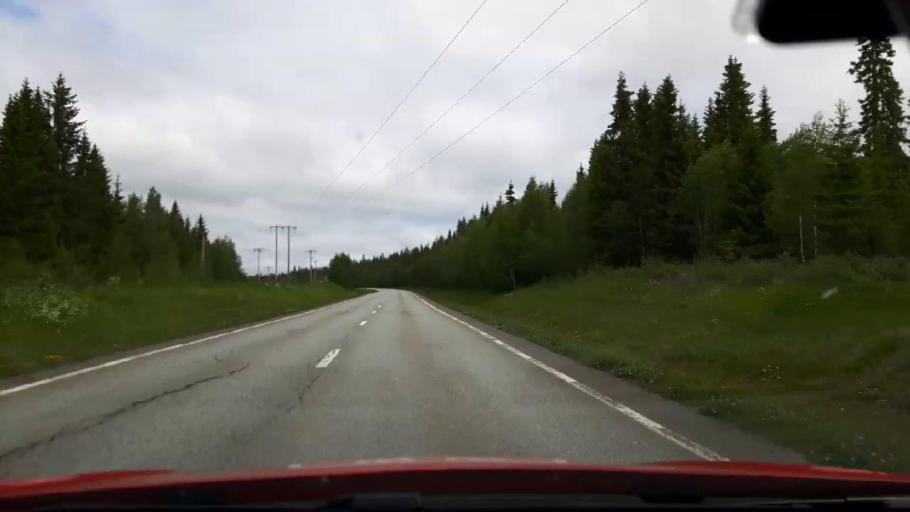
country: SE
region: Jaemtland
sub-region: Krokoms Kommun
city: Krokom
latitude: 63.4707
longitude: 14.4996
